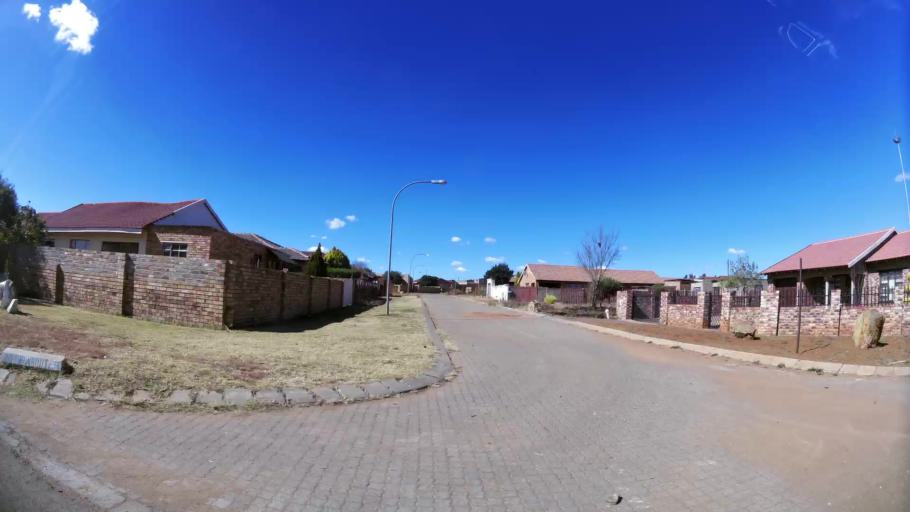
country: ZA
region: North-West
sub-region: Dr Kenneth Kaunda District Municipality
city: Klerksdorp
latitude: -26.8751
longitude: 26.5803
